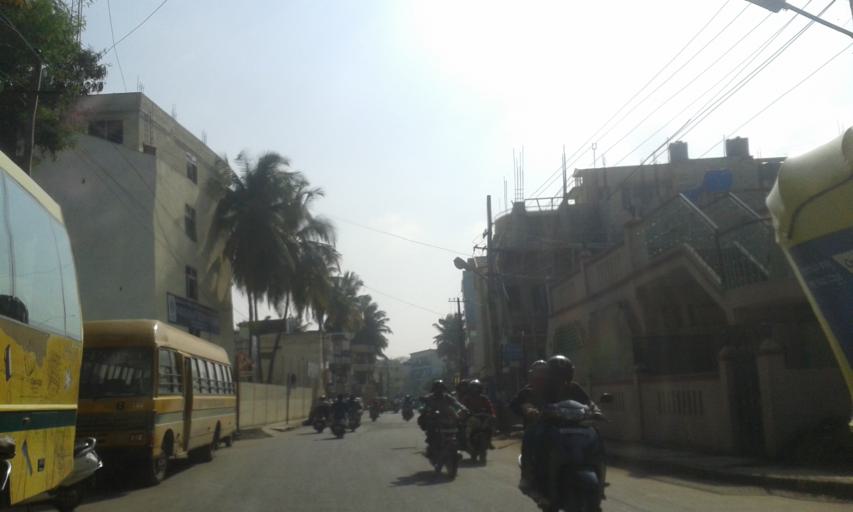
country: IN
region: Karnataka
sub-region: Bangalore Urban
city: Bangalore
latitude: 12.9427
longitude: 77.6140
